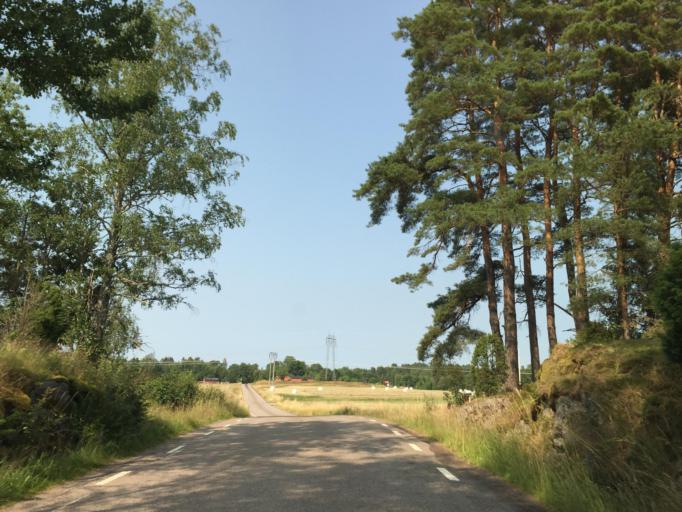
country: SE
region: Vaestra Goetaland
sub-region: Trollhattan
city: Sjuntorp
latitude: 58.3194
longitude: 12.1198
